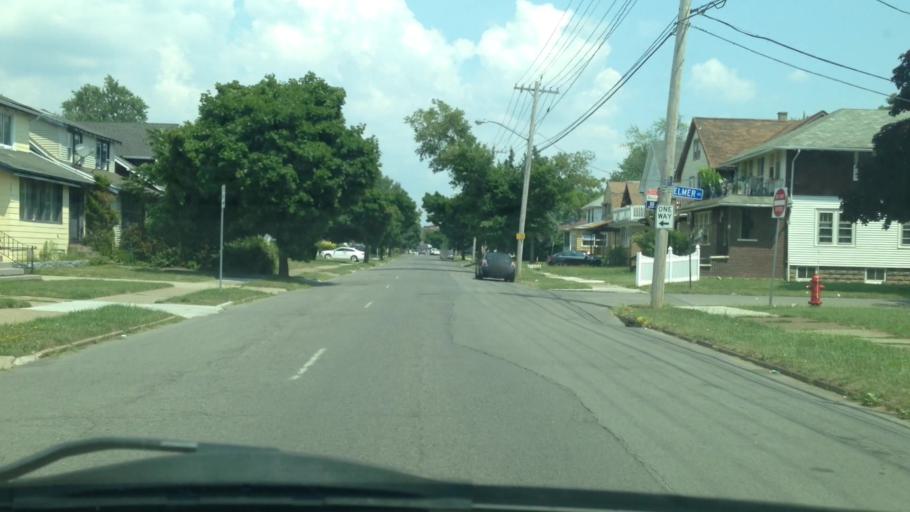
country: US
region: New York
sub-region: Erie County
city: Eggertsville
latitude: 42.9401
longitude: -78.8198
